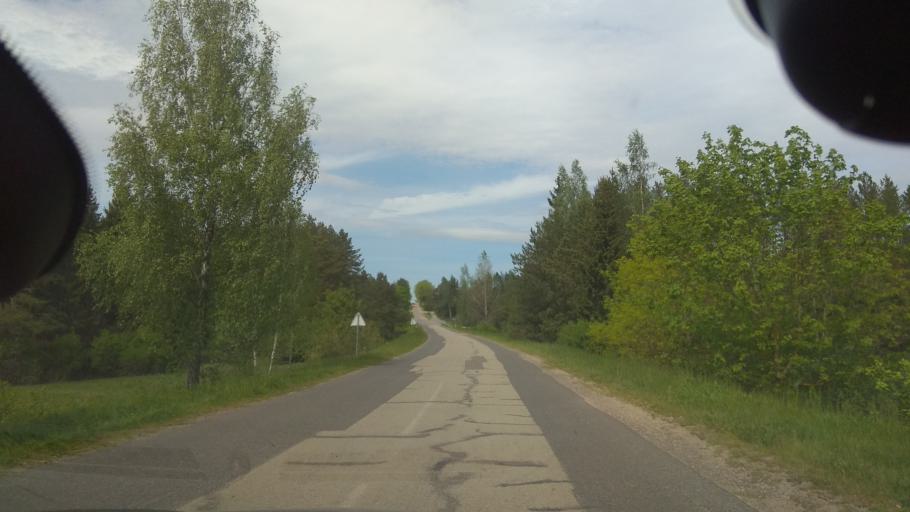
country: LT
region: Vilnius County
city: Ukmerge
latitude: 55.1375
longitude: 24.5938
